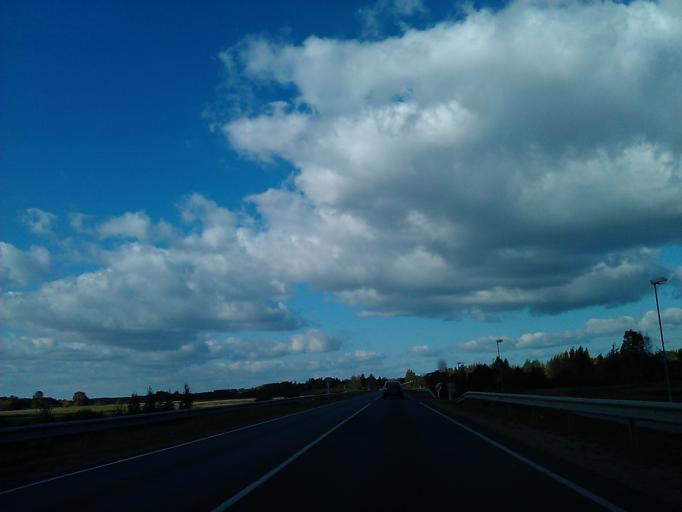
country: LV
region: Livani
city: Livani
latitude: 56.3773
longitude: 26.1622
